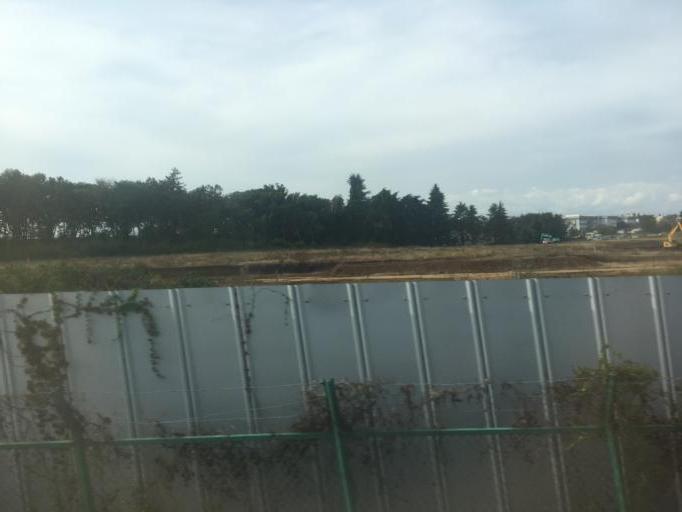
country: JP
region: Saitama
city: Sayama
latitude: 35.8358
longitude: 139.4082
